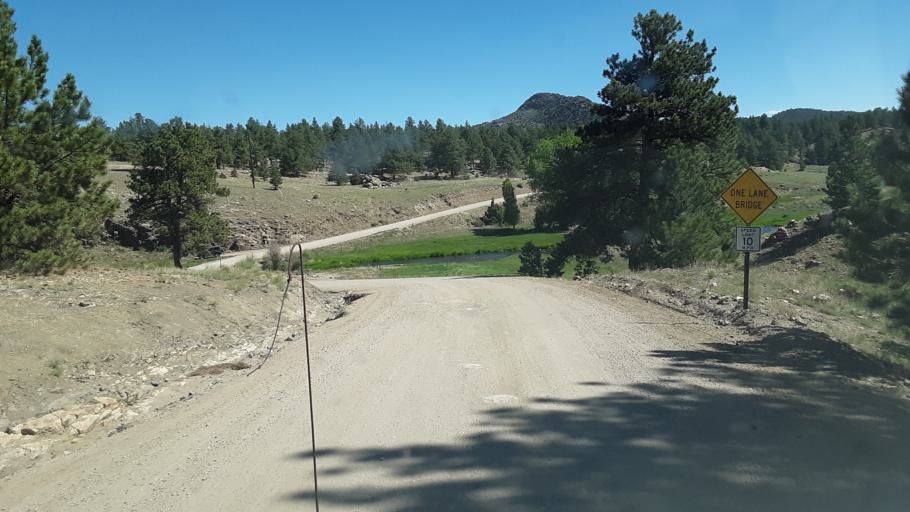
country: US
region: Colorado
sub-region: Custer County
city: Westcliffe
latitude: 38.2104
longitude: -105.4434
